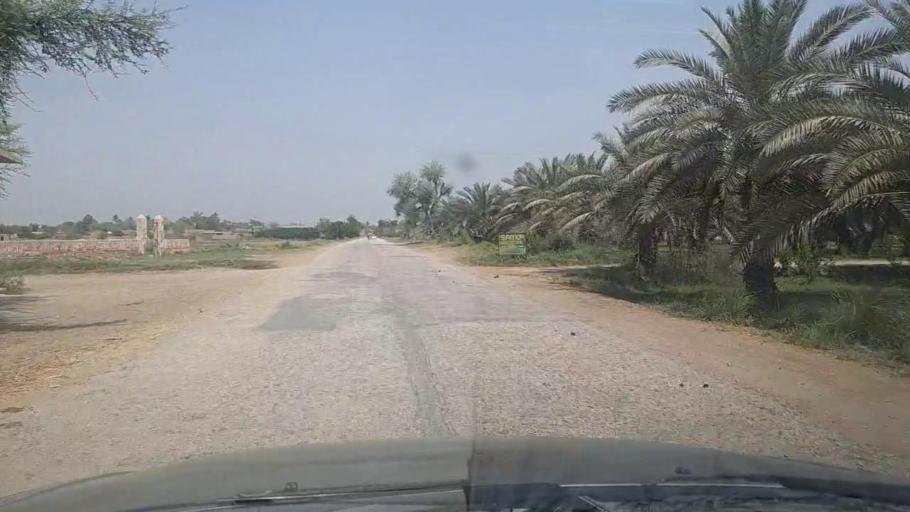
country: PK
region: Sindh
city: Setharja Old
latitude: 27.1633
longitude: 68.5177
